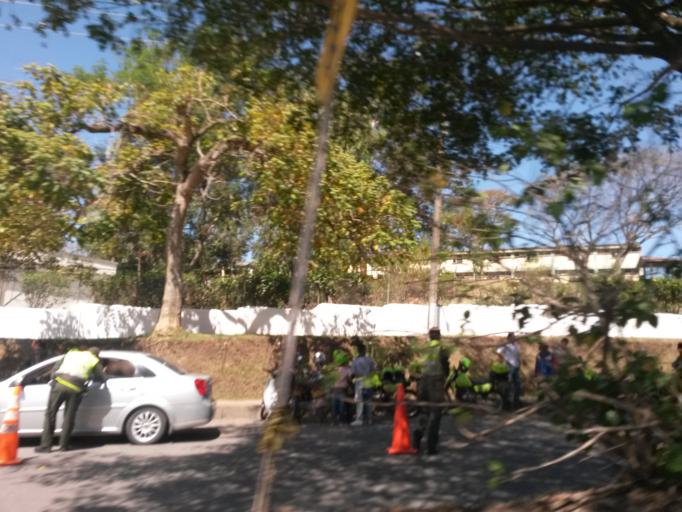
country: CO
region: Cauca
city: Popayan
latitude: 2.4522
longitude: -76.6310
